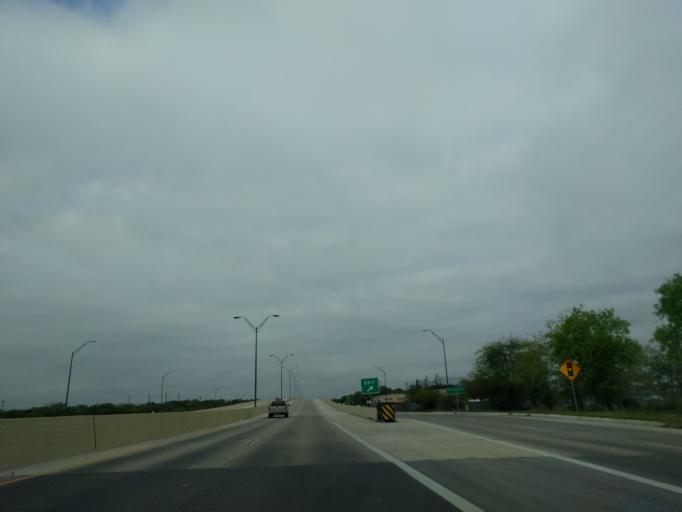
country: US
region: Texas
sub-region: Bexar County
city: Castle Hills
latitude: 29.5466
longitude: -98.4699
